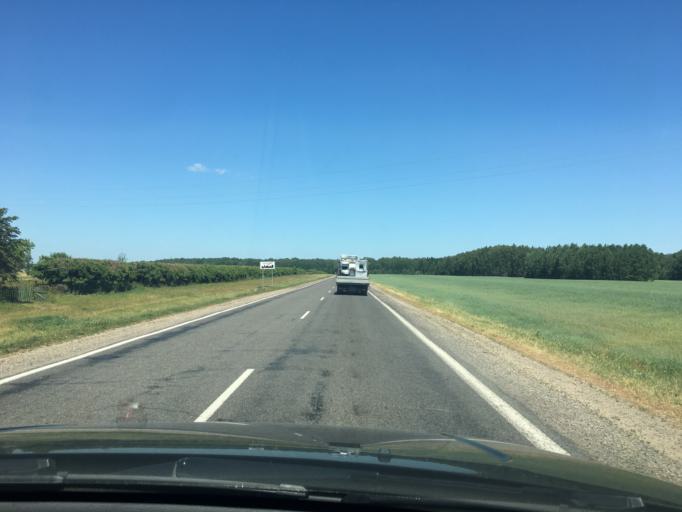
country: BY
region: Grodnenskaya
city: Iwye
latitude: 54.0669
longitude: 25.9117
